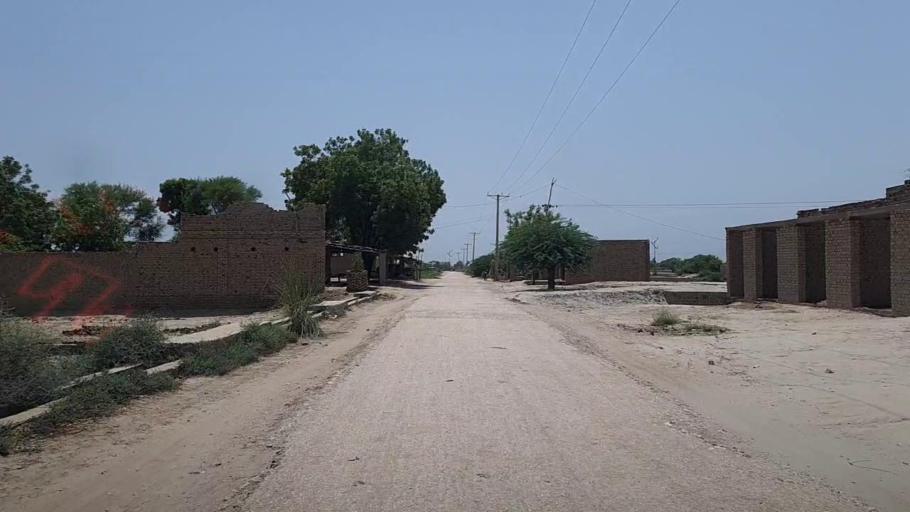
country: PK
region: Sindh
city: Pad Idan
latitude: 26.7741
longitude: 68.2923
